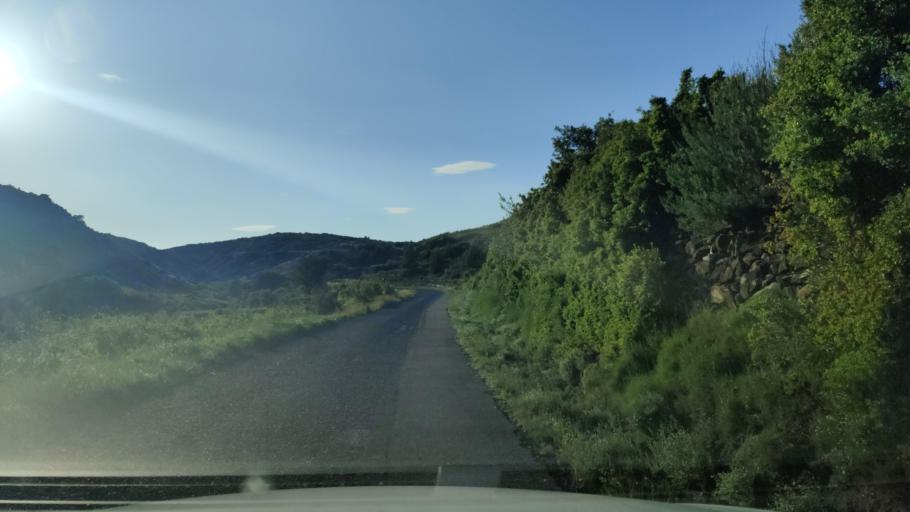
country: FR
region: Languedoc-Roussillon
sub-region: Departement des Pyrenees-Orientales
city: Estagel
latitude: 42.7829
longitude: 2.7558
